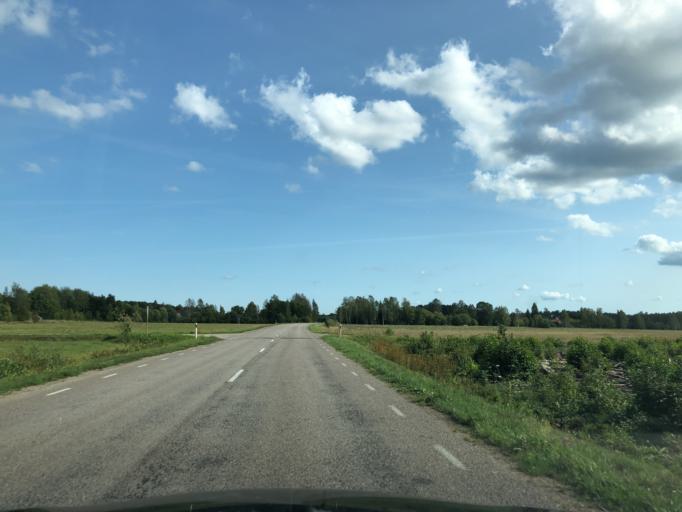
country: EE
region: Hiiumaa
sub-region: Kaerdla linn
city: Kardla
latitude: 58.7168
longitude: 22.5702
